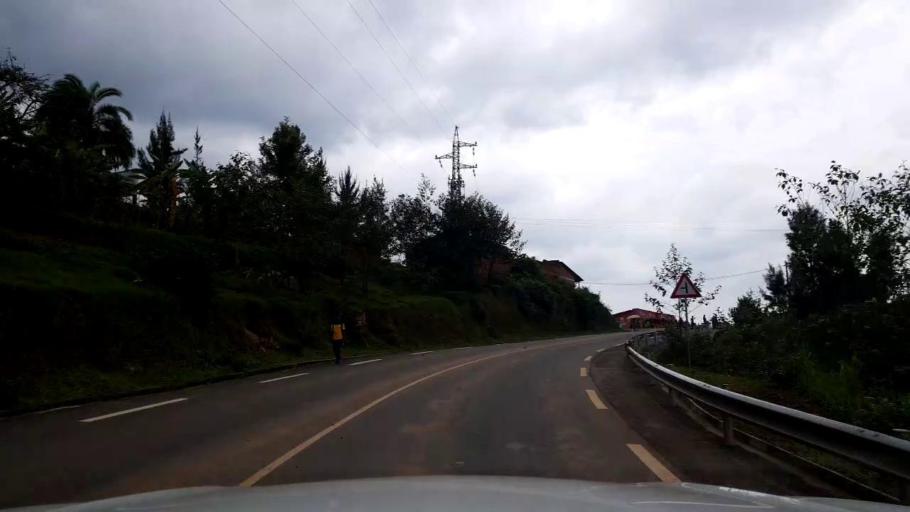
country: RW
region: Western Province
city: Kibuye
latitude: -1.8830
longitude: 29.3497
